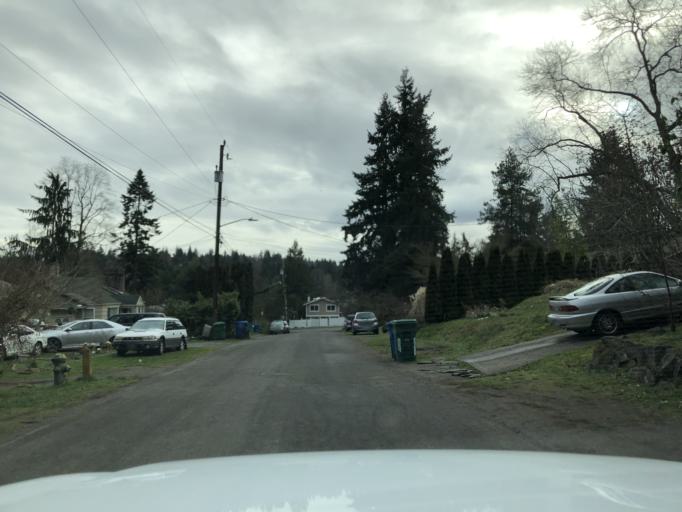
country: US
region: Washington
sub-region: King County
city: Lake Forest Park
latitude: 47.7094
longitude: -122.2980
